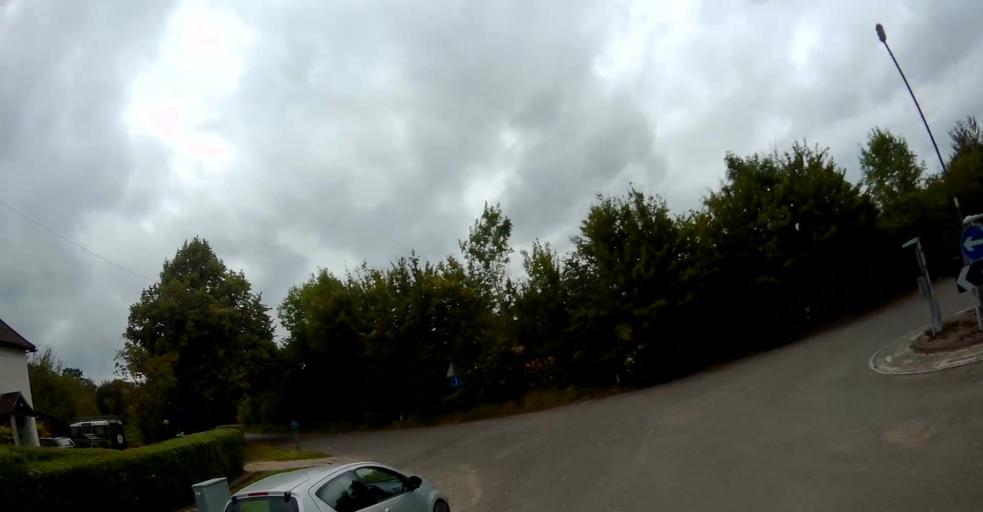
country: GB
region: England
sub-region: Hampshire
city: Aldershot
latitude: 51.2227
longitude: -0.7549
